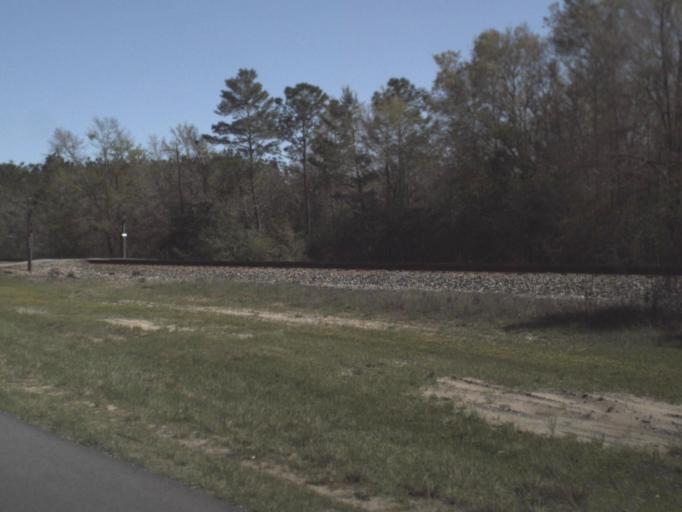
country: US
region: Florida
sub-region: Walton County
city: DeFuniak Springs
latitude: 30.7403
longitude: -86.1832
